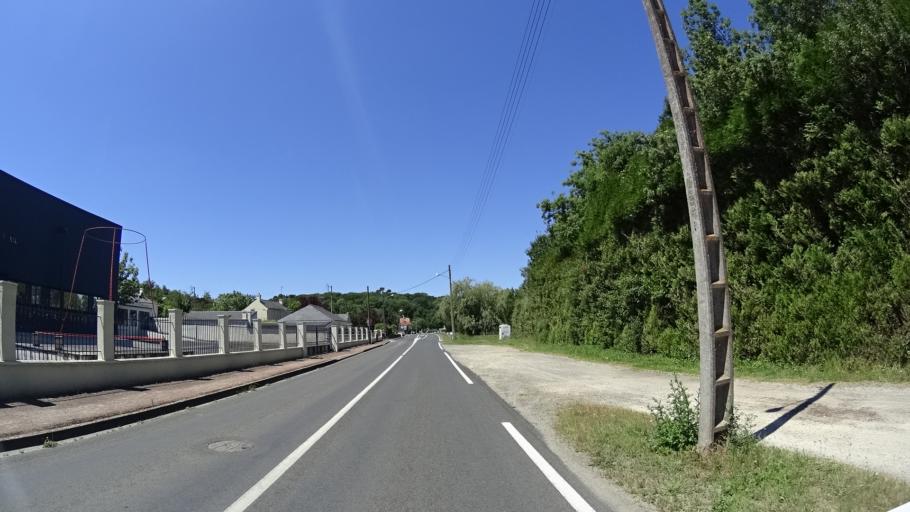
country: FR
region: Pays de la Loire
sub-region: Departement de Maine-et-Loire
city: Saumur
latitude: 47.2782
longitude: -0.1167
